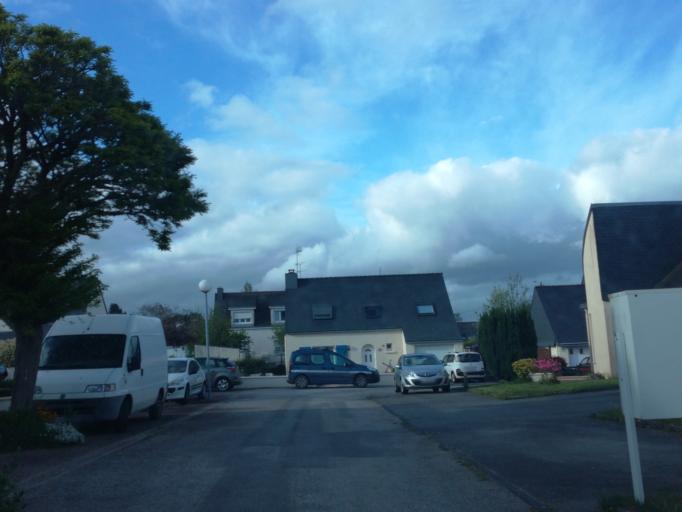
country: FR
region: Brittany
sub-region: Departement du Morbihan
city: Le Sourn
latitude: 48.0410
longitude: -2.9880
